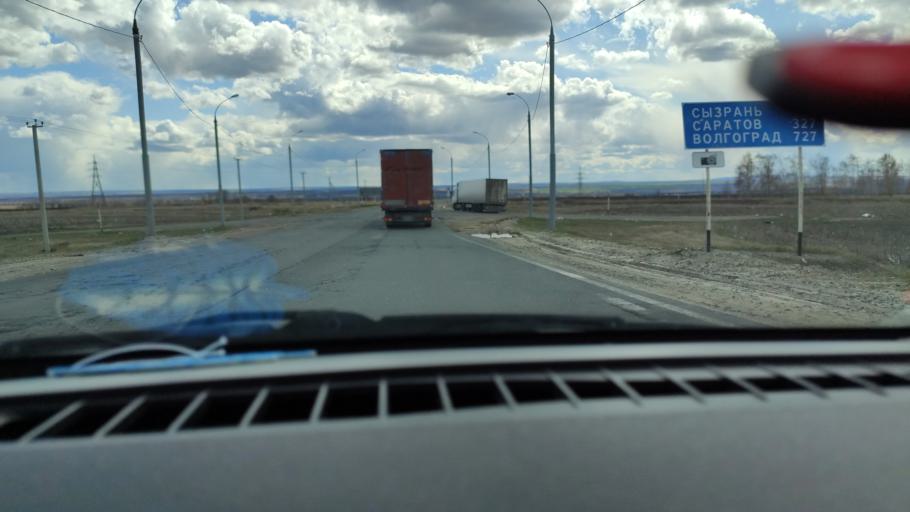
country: RU
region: Samara
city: Varlamovo
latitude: 53.1865
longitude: 48.2908
